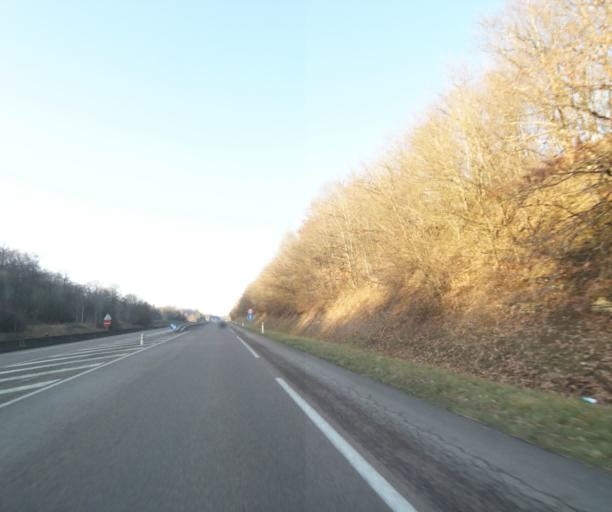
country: FR
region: Champagne-Ardenne
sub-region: Departement de la Haute-Marne
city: Chevillon
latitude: 48.5031
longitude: 5.1034
